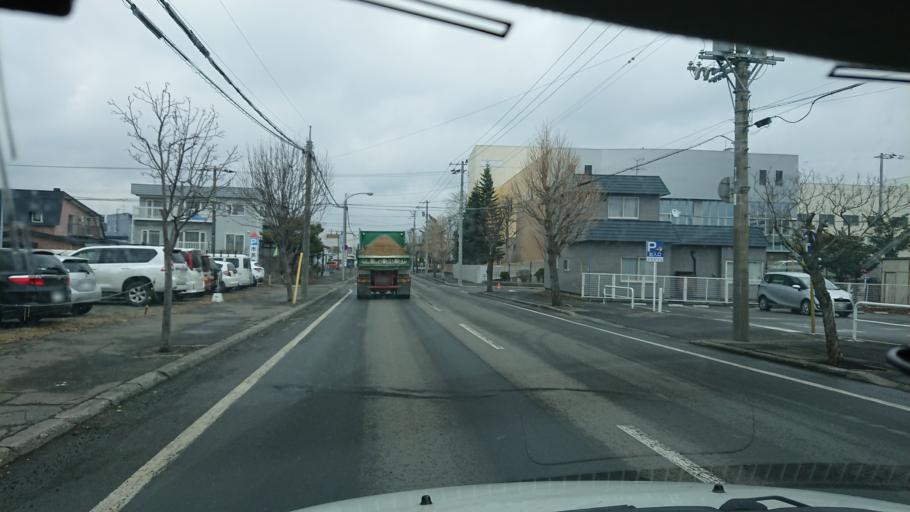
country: JP
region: Hokkaido
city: Kitahiroshima
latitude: 42.8830
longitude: 141.5756
